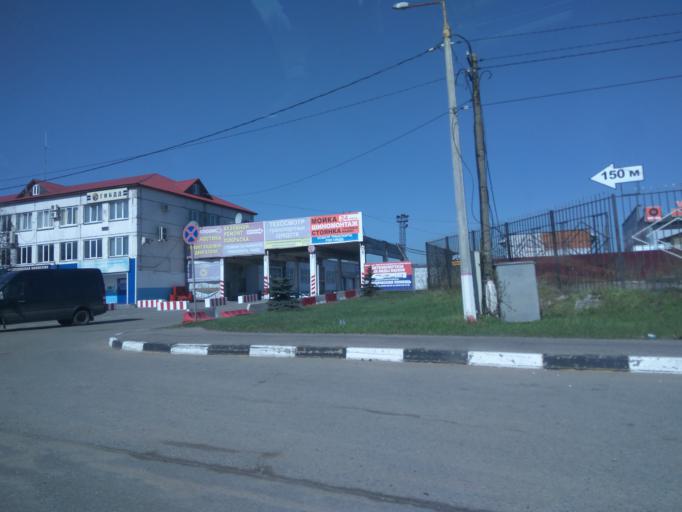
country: RU
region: Moskovskaya
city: Ramenskoye
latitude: 55.5606
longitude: 38.2621
